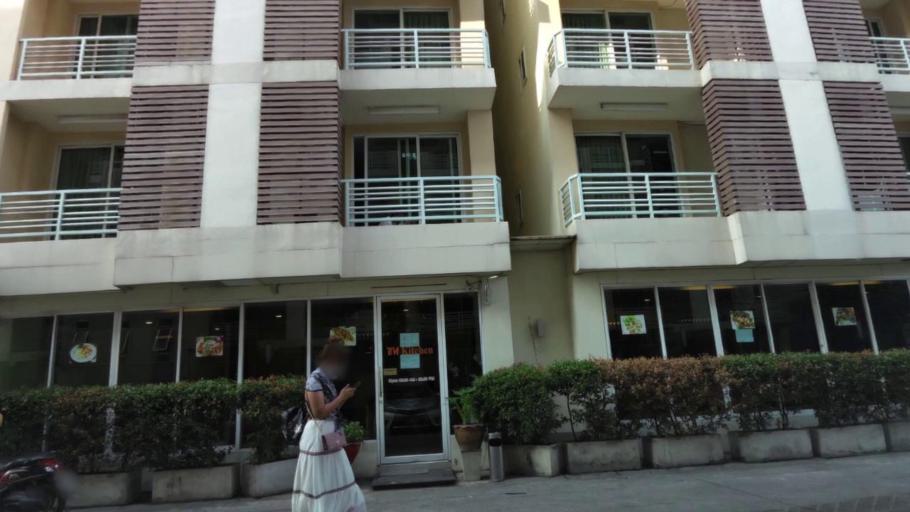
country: TH
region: Phra Nakhon Si Ayutthaya
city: Uthai
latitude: 14.3211
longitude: 100.6303
